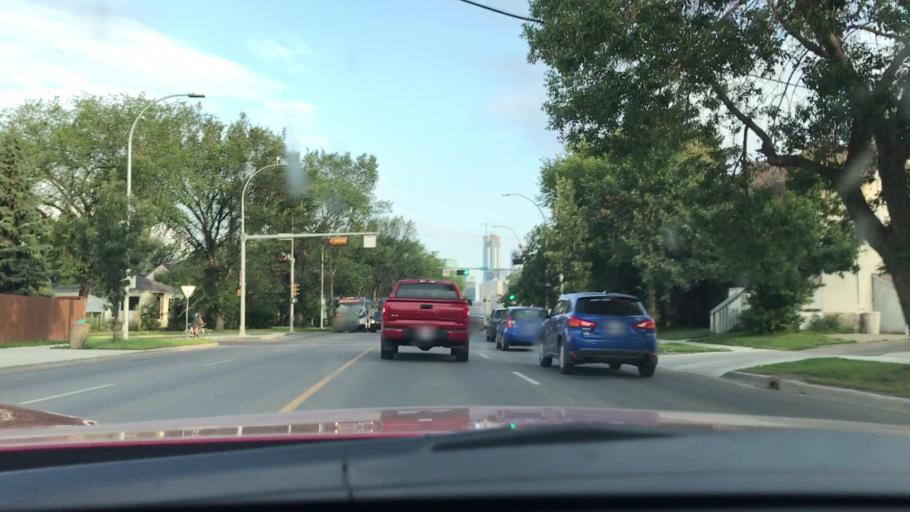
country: CA
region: Alberta
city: Edmonton
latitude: 53.5297
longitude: -113.4675
